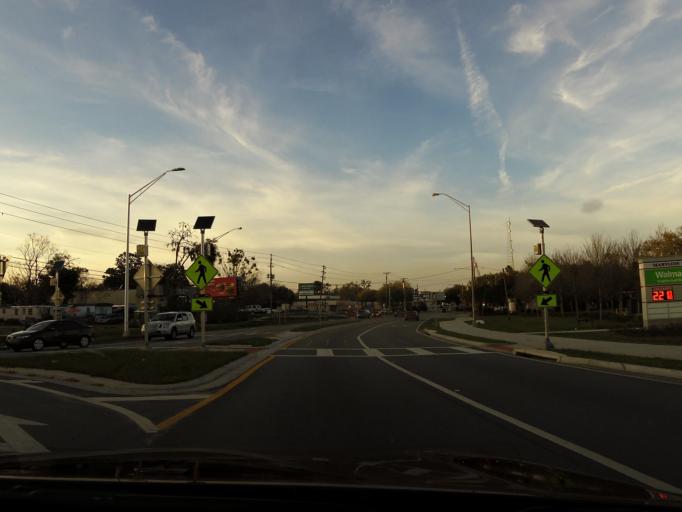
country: US
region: Florida
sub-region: Volusia County
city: De Land Southwest
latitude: 29.0121
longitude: -81.3026
